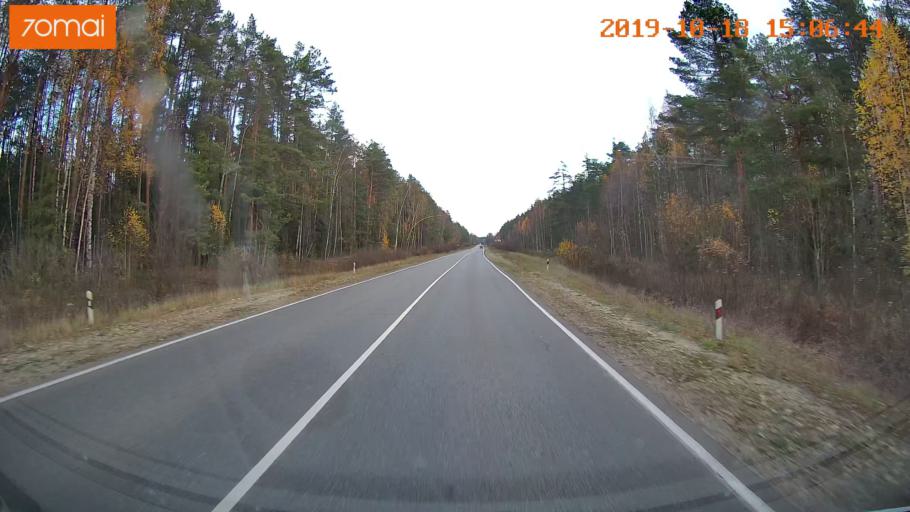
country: RU
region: Vladimir
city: Gus'-Khrustal'nyy
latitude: 55.5338
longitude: 40.5819
